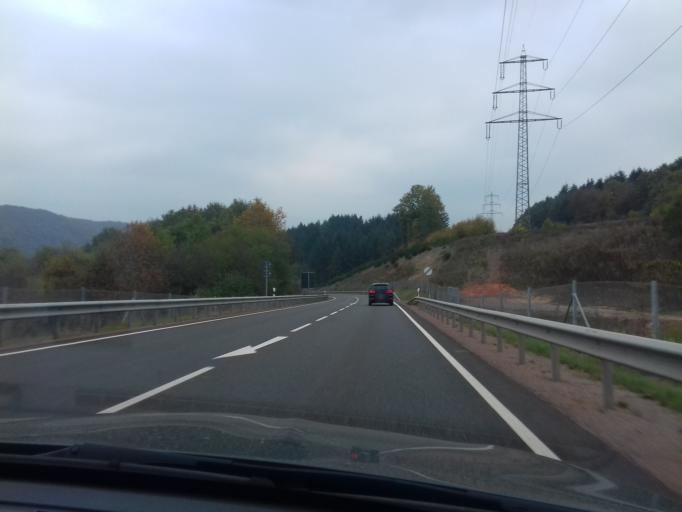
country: DE
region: Rheinland-Pfalz
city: Tawern
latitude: 49.6764
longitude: 6.5390
